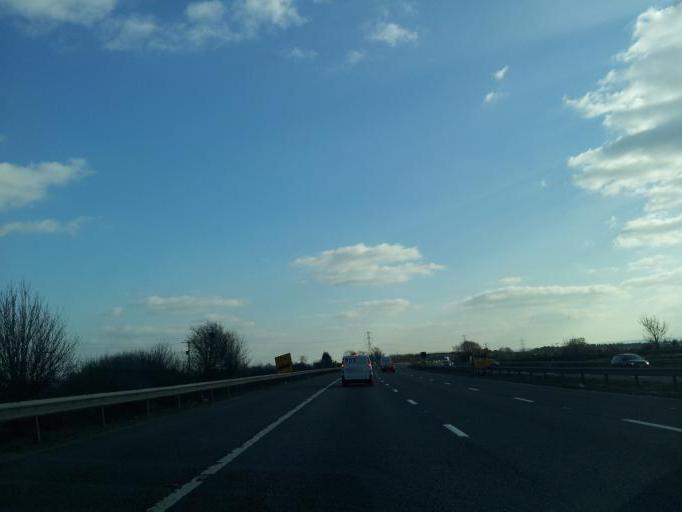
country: GB
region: England
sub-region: Somerset
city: Bridgwater
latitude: 51.1335
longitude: -2.9679
